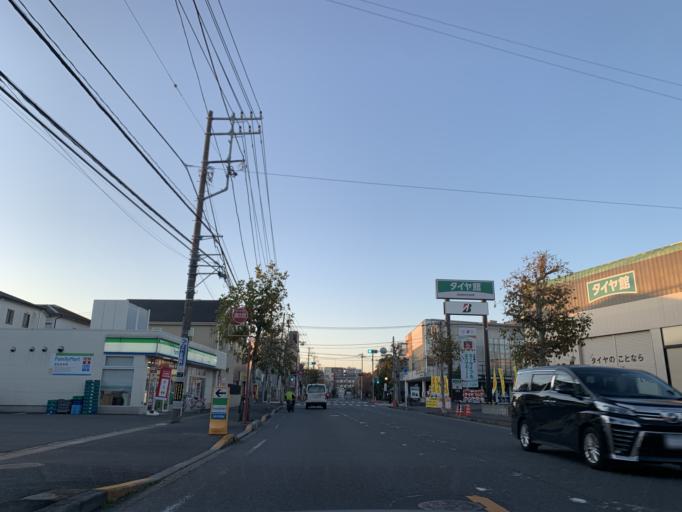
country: JP
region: Tokyo
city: Urayasu
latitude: 35.7171
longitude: 139.9114
